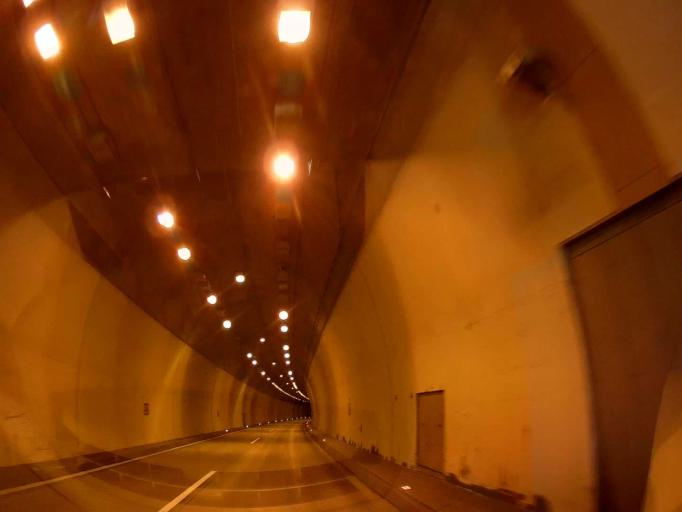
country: AT
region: Styria
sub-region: Politischer Bezirk Graz-Umgebung
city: Deutschfeistritz
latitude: 47.2015
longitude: 15.3233
